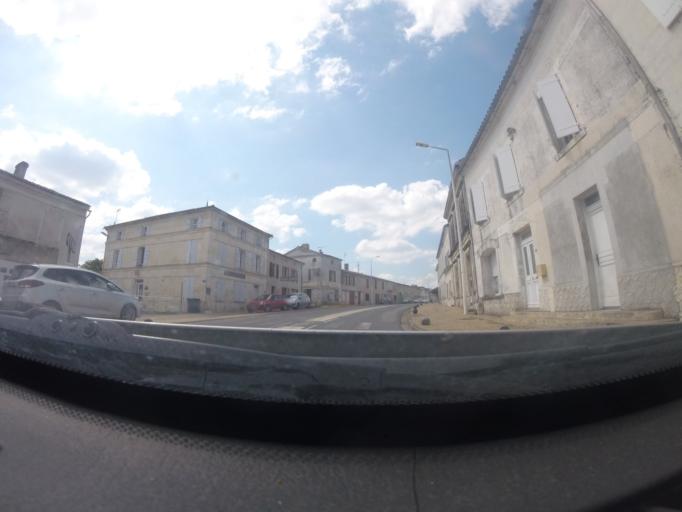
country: FR
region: Poitou-Charentes
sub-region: Departement de la Charente-Maritime
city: Bords
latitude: 45.8605
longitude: -0.8363
